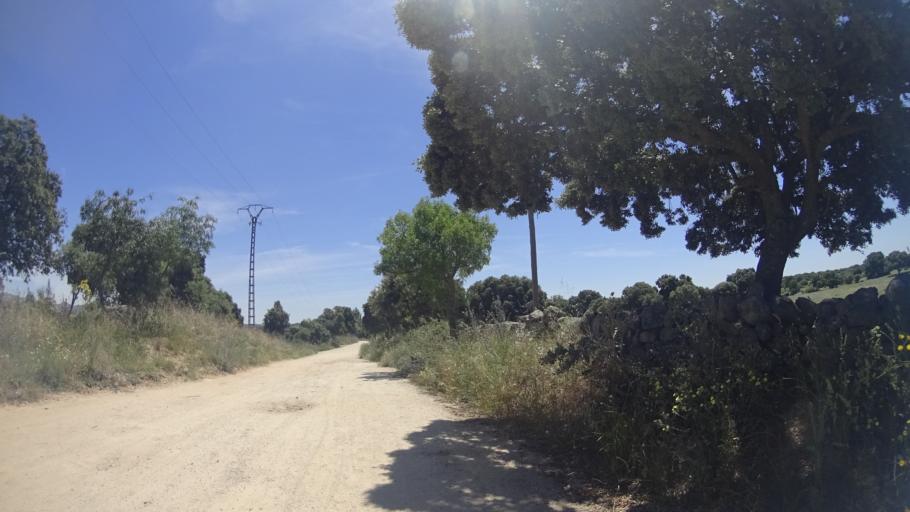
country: ES
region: Madrid
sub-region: Provincia de Madrid
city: Navalquejigo
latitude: 40.6109
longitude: -4.0350
